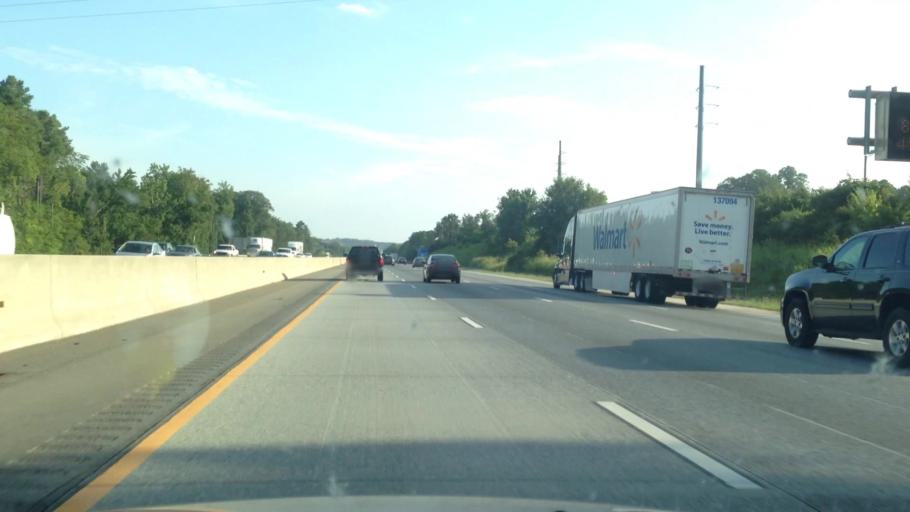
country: US
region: North Carolina
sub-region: Cabarrus County
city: Harrisburg
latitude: 35.3953
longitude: -80.7011
